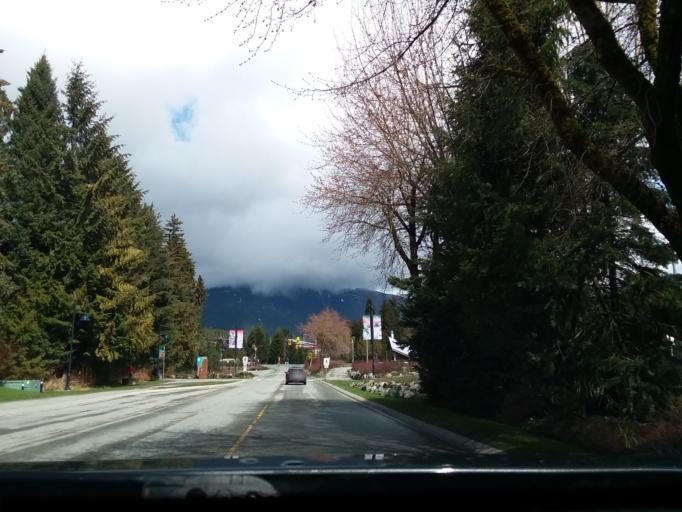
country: CA
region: British Columbia
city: Whistler
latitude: 50.1185
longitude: -122.9539
